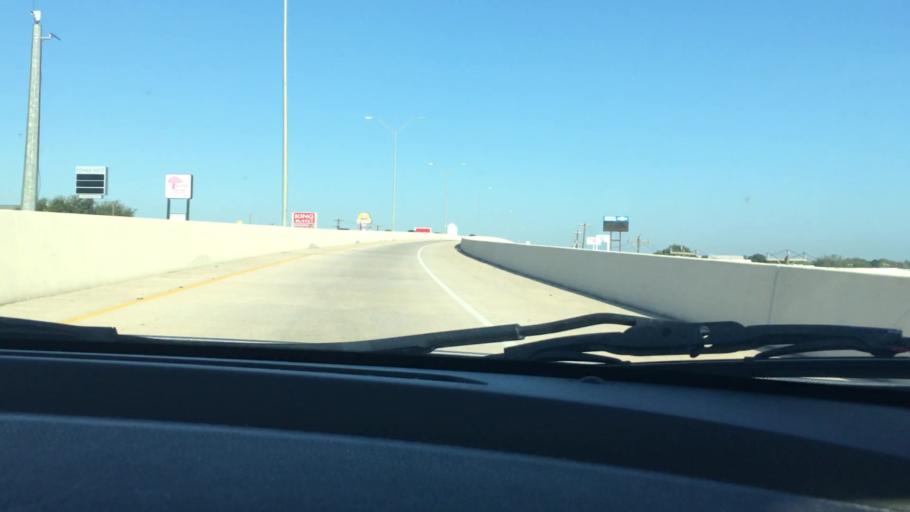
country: US
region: Texas
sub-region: Bexar County
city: Leon Valley
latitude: 29.4845
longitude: -98.6046
